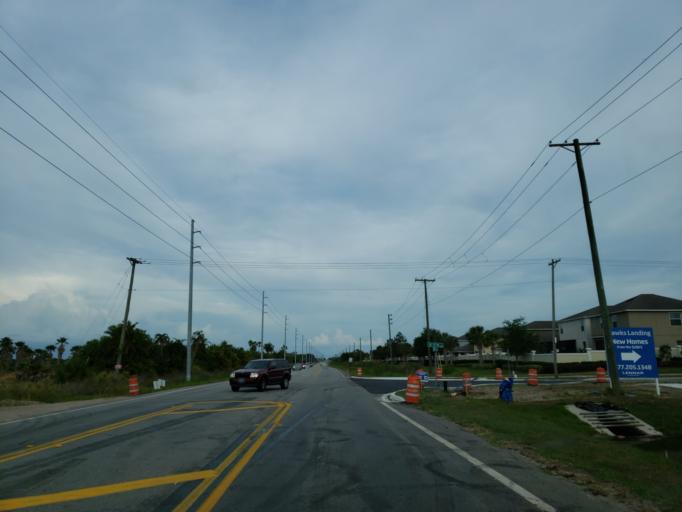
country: US
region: Florida
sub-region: Hillsborough County
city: Ruskin
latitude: 27.7350
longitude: -82.4109
